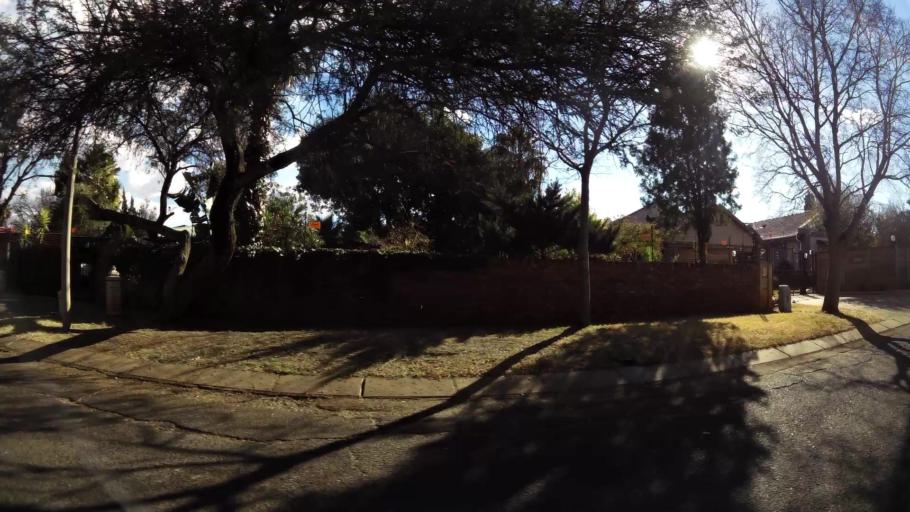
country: ZA
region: North-West
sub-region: Dr Kenneth Kaunda District Municipality
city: Klerksdorp
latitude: -26.8291
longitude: 26.6806
